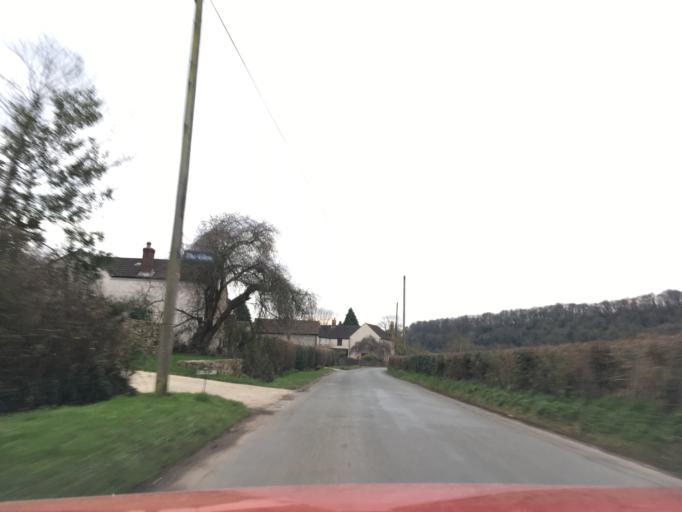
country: GB
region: Wales
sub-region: Newport
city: Llanvaches
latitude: 51.6081
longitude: -2.8270
